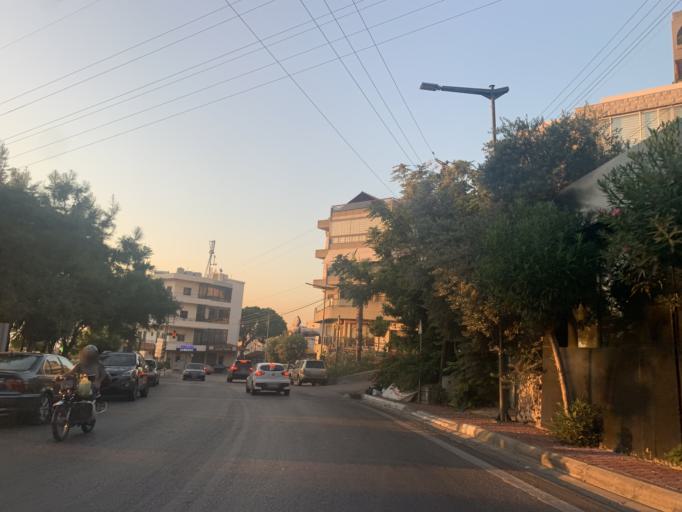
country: LB
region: Mont-Liban
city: Djounie
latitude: 33.9632
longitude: 35.6242
